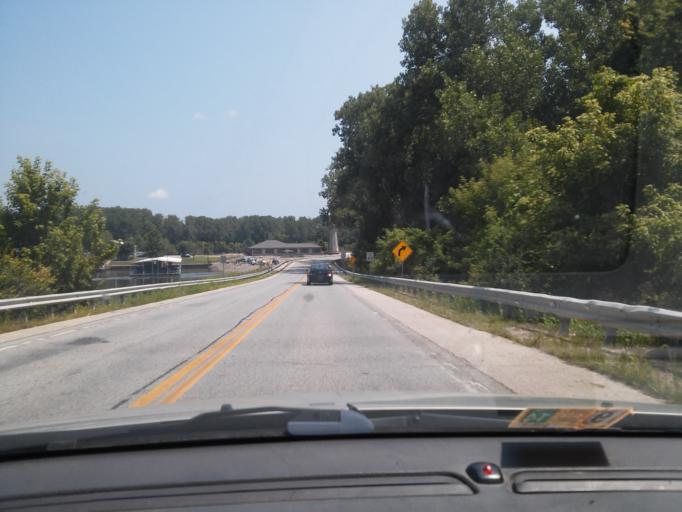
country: US
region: Missouri
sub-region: Pike County
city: Louisiana
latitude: 39.4588
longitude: -91.0433
